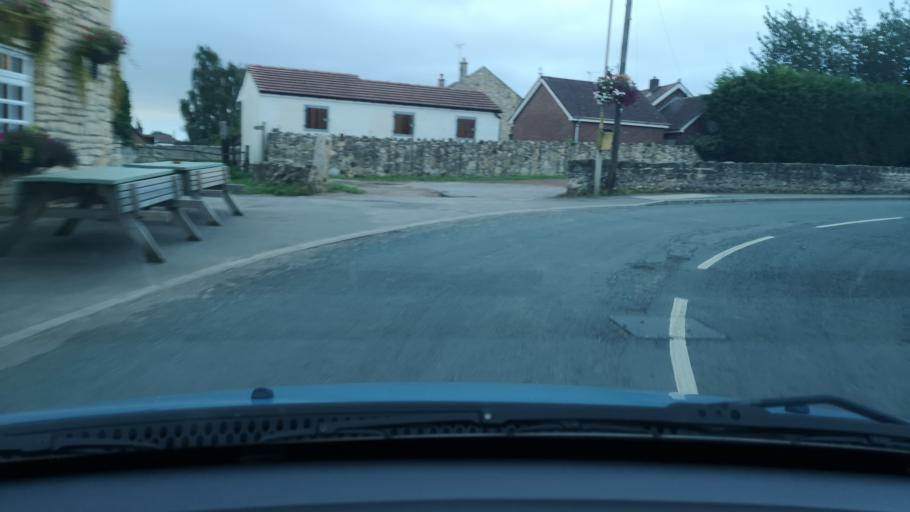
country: GB
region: England
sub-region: Doncaster
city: Norton
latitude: 53.6437
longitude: -1.2160
